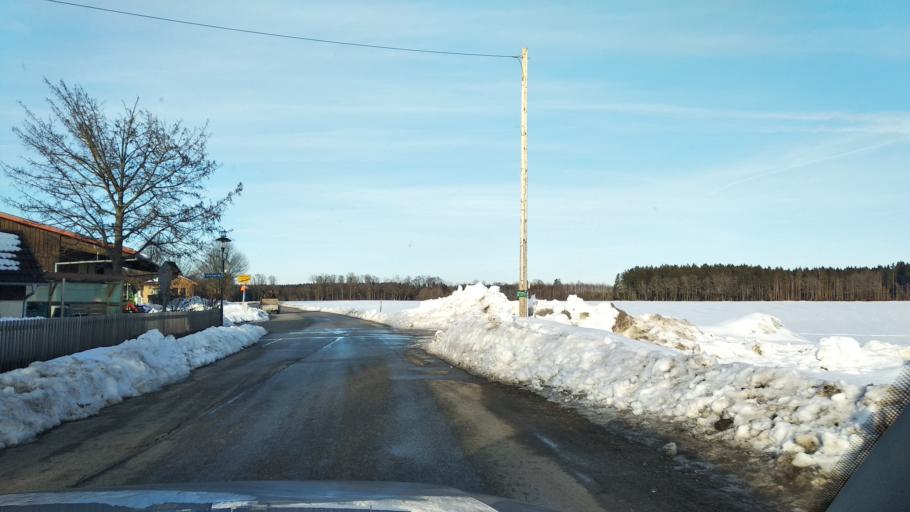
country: DE
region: Bavaria
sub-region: Upper Bavaria
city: Zorneding
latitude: 48.0619
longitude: 11.8527
